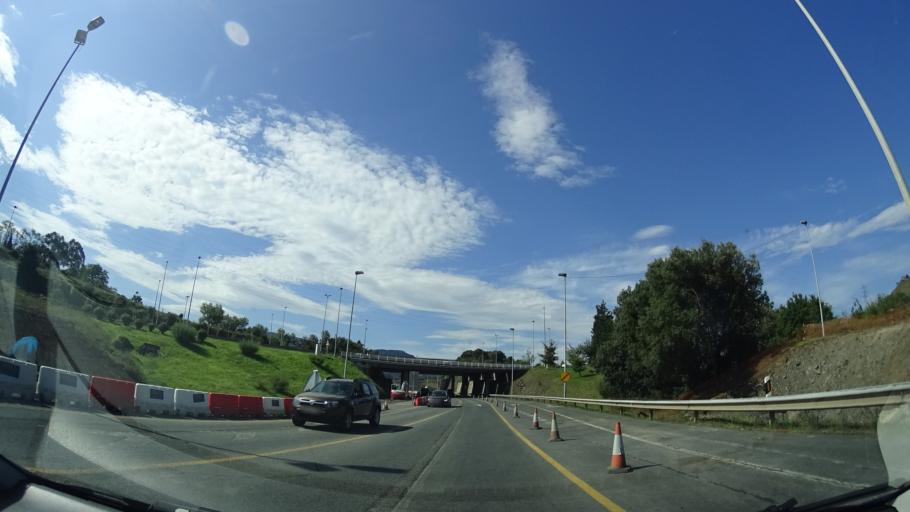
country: ES
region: Basque Country
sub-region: Bizkaia
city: Zierbena
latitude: 43.3308
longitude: -3.0796
